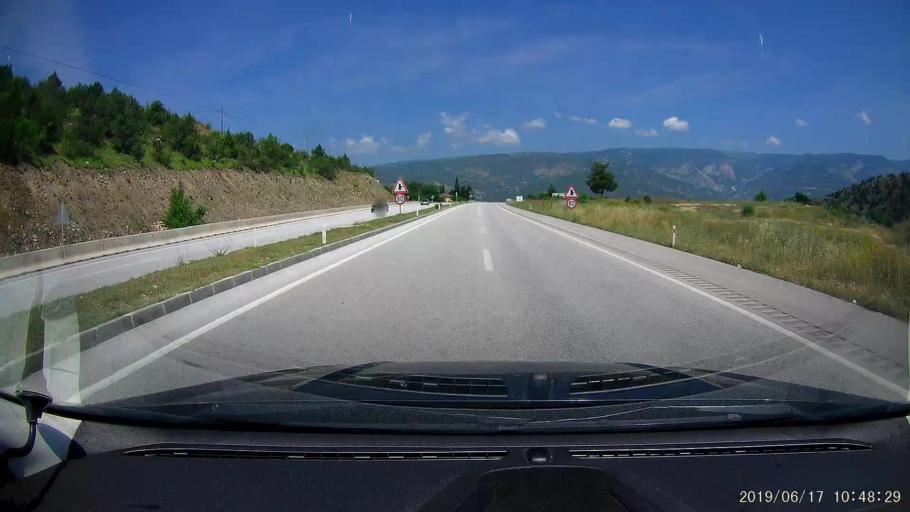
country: TR
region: Corum
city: Hacihamza
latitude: 41.0894
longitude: 34.4277
